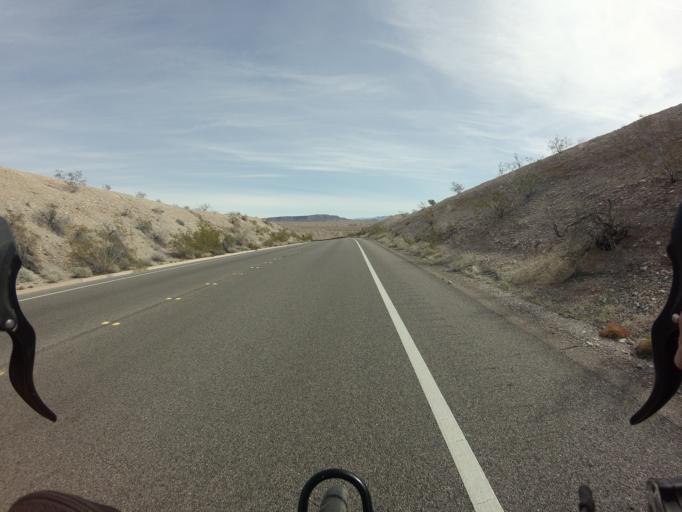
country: US
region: Nevada
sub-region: Clark County
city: Henderson
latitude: 36.1466
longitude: -114.8524
